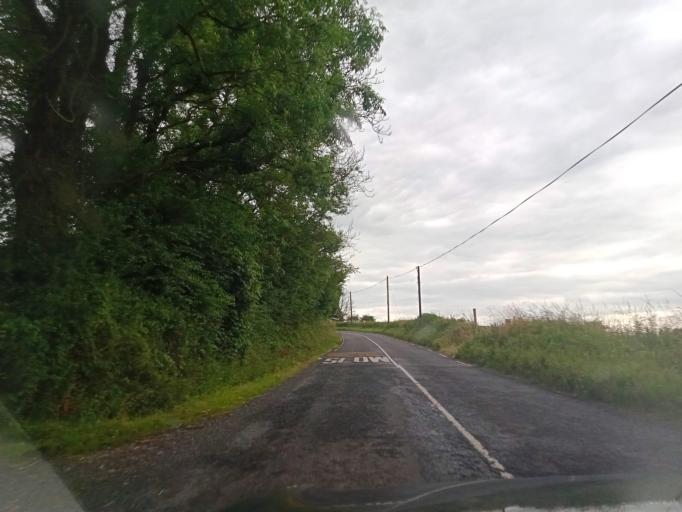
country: IE
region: Leinster
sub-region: Laois
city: Stradbally
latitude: 52.9239
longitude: -7.1935
